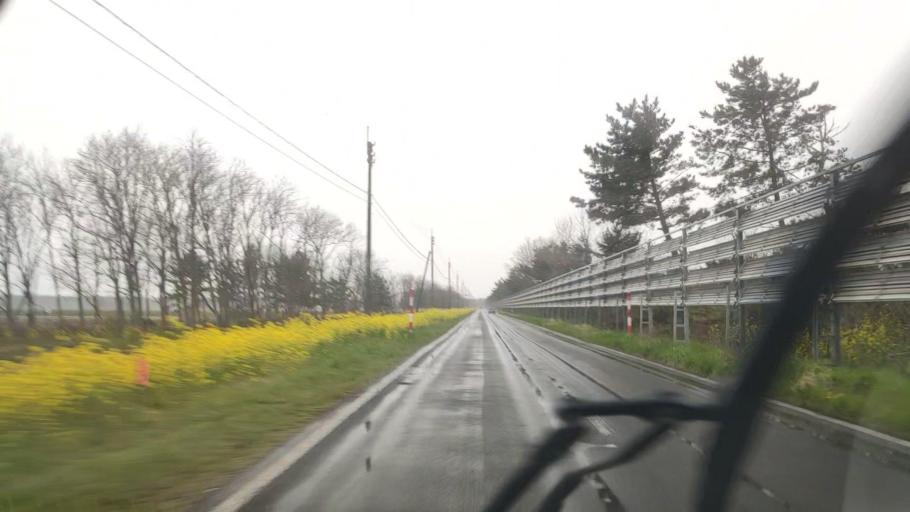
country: JP
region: Akita
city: Tenno
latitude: 40.0439
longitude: 139.9572
